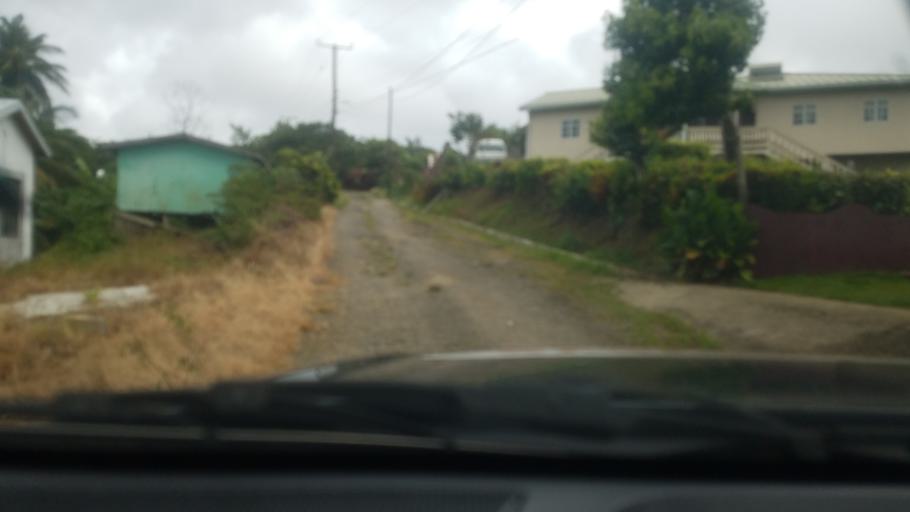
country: LC
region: Micoud Quarter
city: Micoud
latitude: 13.8049
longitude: -60.9428
